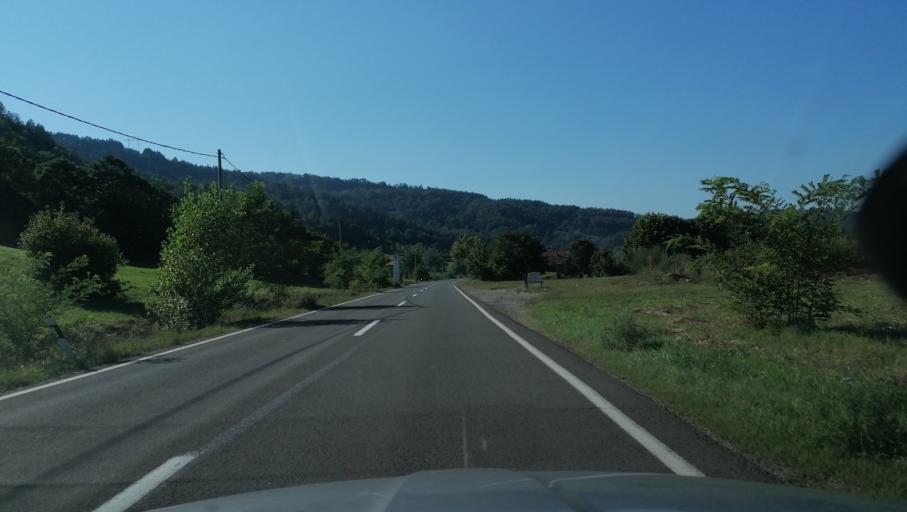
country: RS
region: Central Serbia
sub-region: Raski Okrug
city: Kraljevo
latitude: 43.6699
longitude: 20.5798
